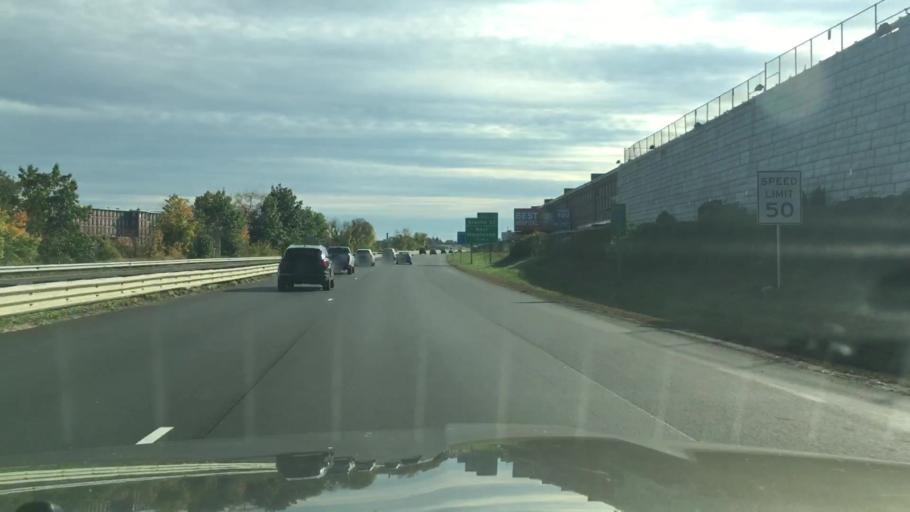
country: US
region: New Hampshire
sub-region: Hillsborough County
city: Manchester
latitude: 42.9937
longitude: -71.4708
